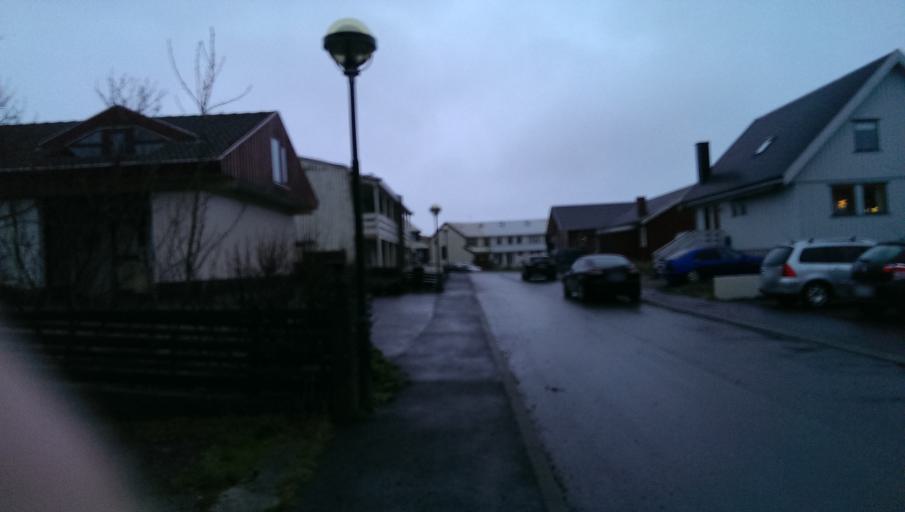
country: FO
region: Streymoy
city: Hoyvik
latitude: 62.0349
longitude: -6.7909
